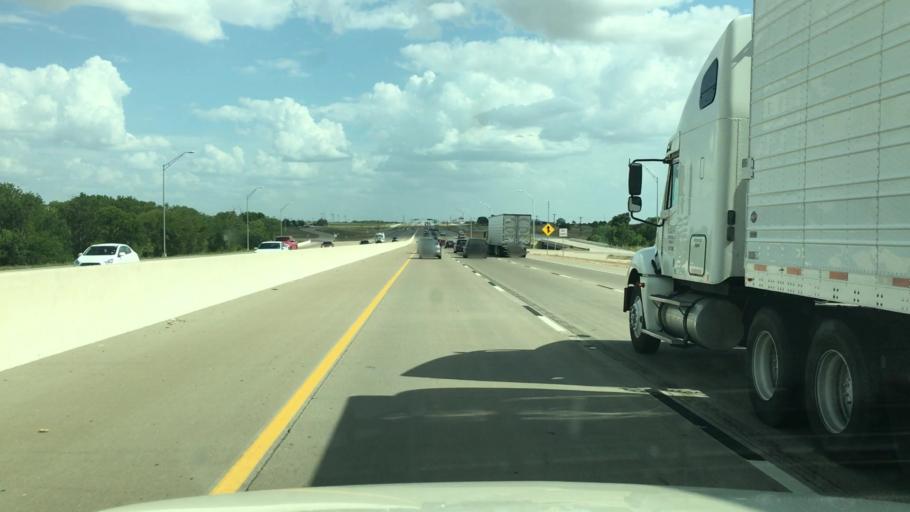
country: US
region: Texas
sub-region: Hill County
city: Hillsboro
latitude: 31.9229
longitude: -97.1005
